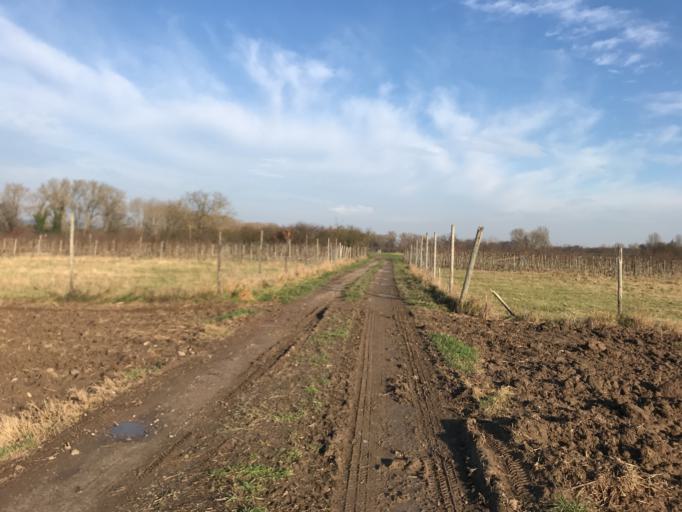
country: DE
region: Hesse
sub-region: Regierungsbezirk Darmstadt
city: Eltville
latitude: 50.0127
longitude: 8.1290
